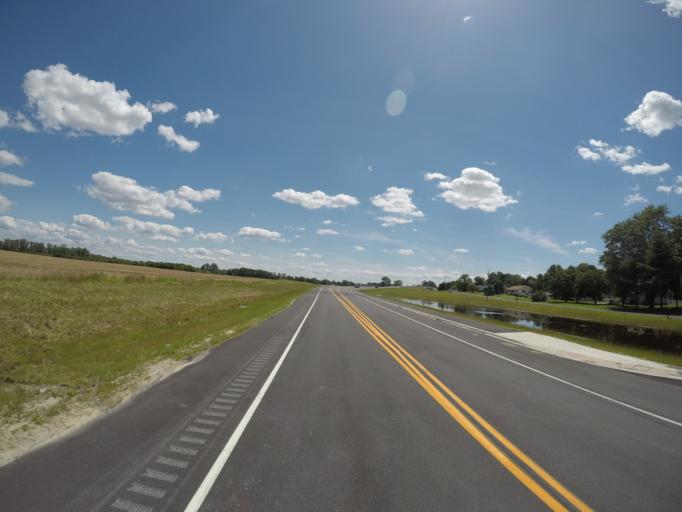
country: US
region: Delaware
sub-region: Sussex County
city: Milford
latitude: 38.9290
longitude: -75.4096
